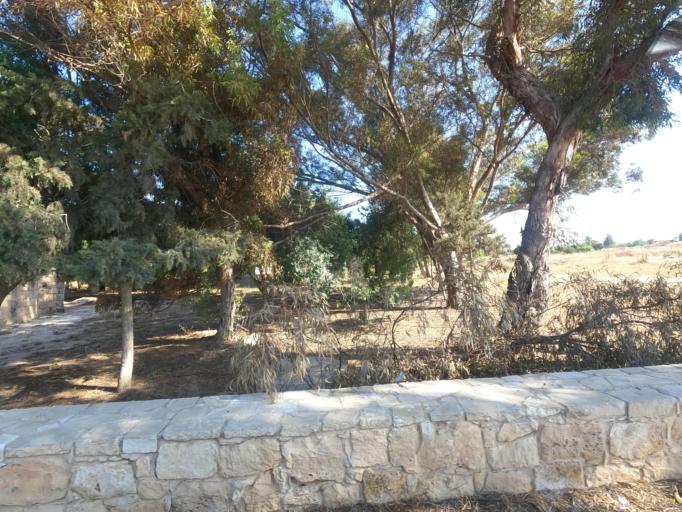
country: CY
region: Ammochostos
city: Frenaros
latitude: 35.0452
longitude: 33.9378
